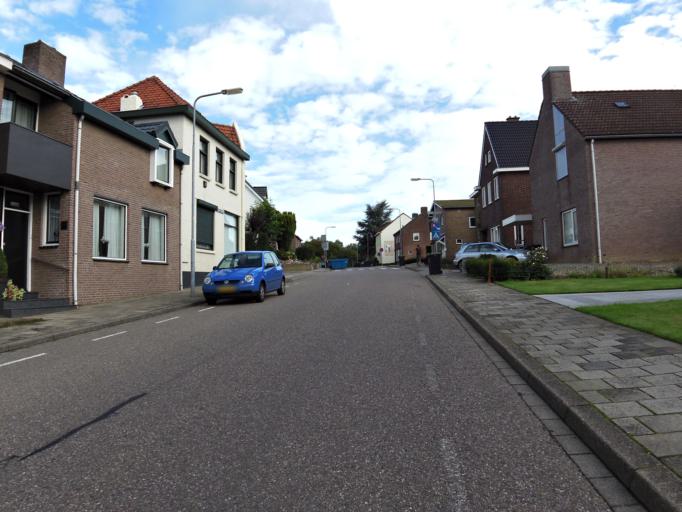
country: NL
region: Limburg
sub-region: Gemeente Nuth
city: Nuth
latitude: 50.9042
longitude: 5.8843
